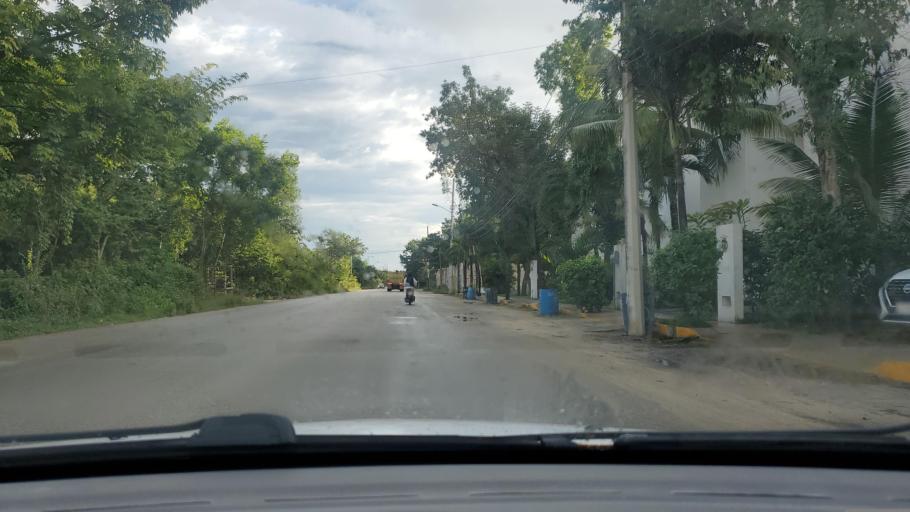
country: MX
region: Quintana Roo
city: Tulum
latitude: 20.2099
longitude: -87.4773
